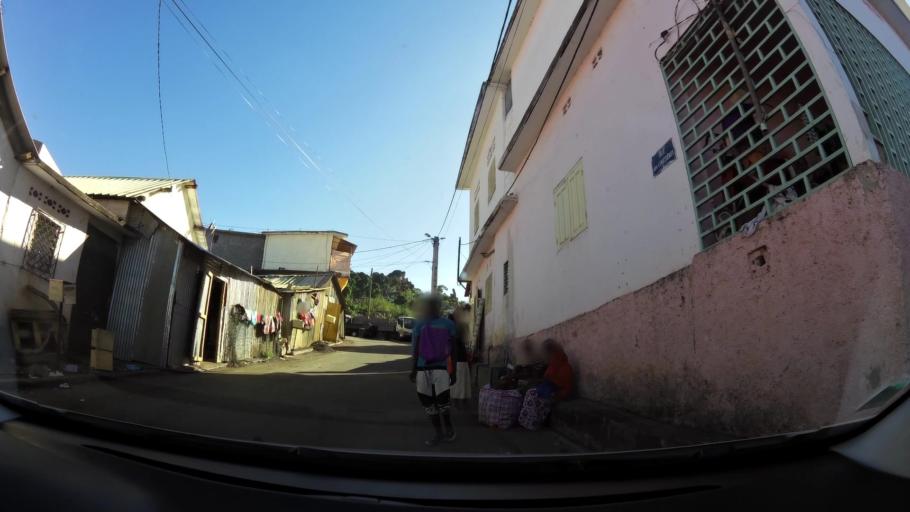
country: YT
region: Mamoudzou
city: Mamoudzou
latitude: -12.7734
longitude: 45.2193
